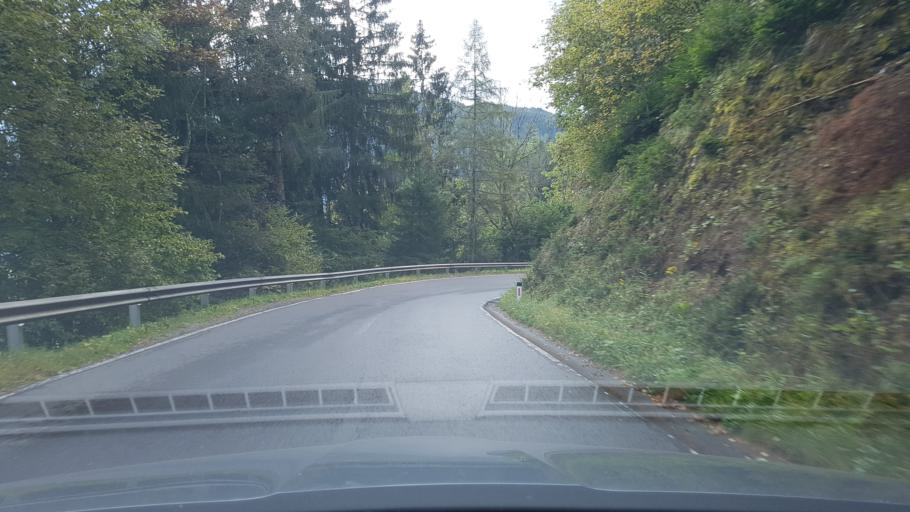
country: AT
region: Styria
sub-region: Politischer Bezirk Murau
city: Schoder
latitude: 47.1945
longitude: 14.1212
